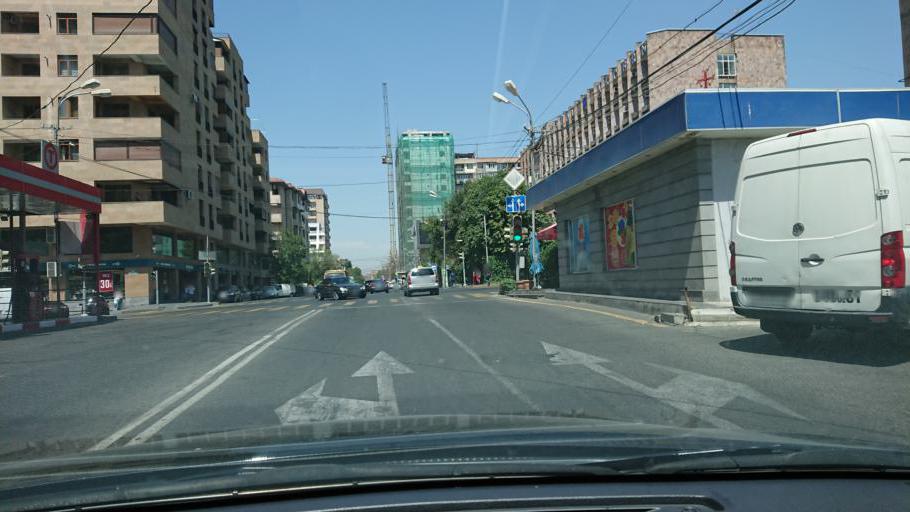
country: AM
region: Yerevan
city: Yerevan
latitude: 40.1984
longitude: 44.5018
